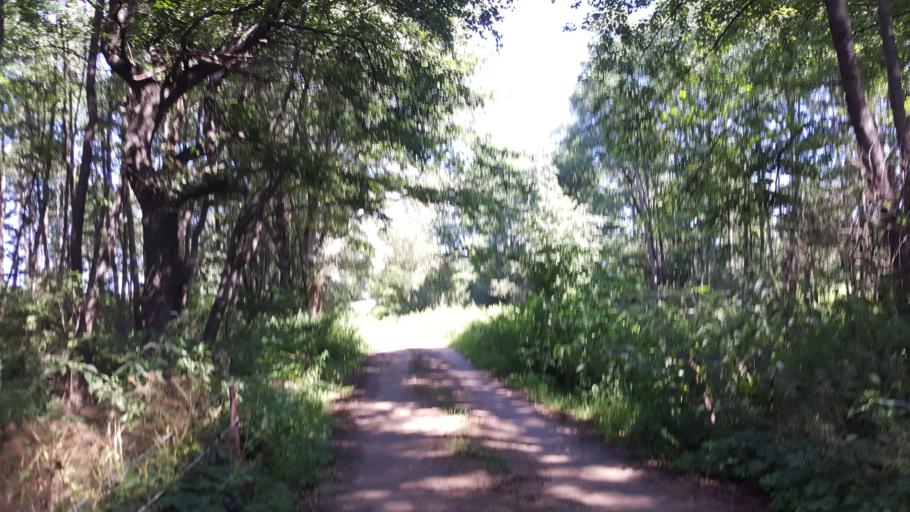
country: BY
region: Brest
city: Charnawchytsy
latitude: 52.3427
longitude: 23.6268
